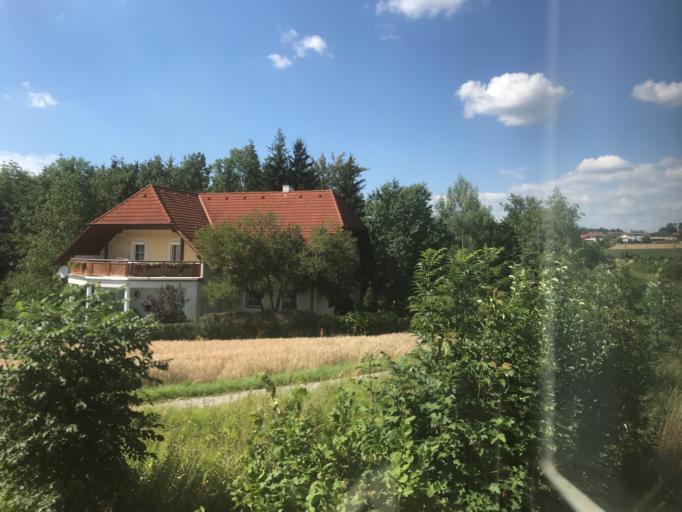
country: AT
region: Upper Austria
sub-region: Politischer Bezirk Urfahr-Umgebung
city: Engerwitzdorf
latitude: 48.3251
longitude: 14.5142
